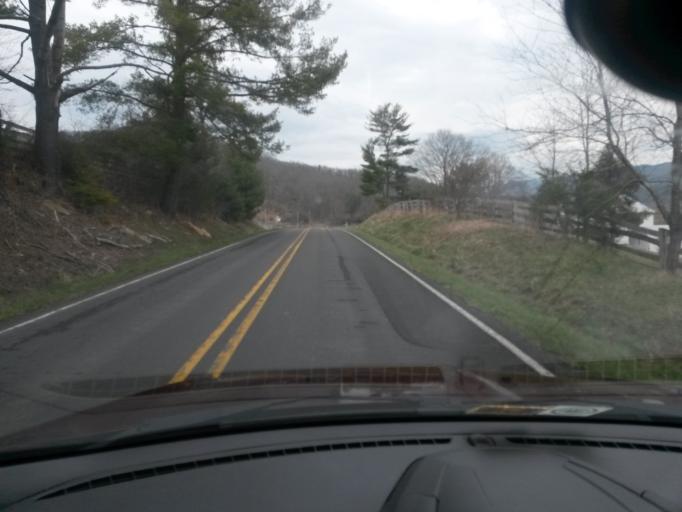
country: US
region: Virginia
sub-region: Bath County
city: Warm Springs
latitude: 38.2078
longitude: -79.7234
